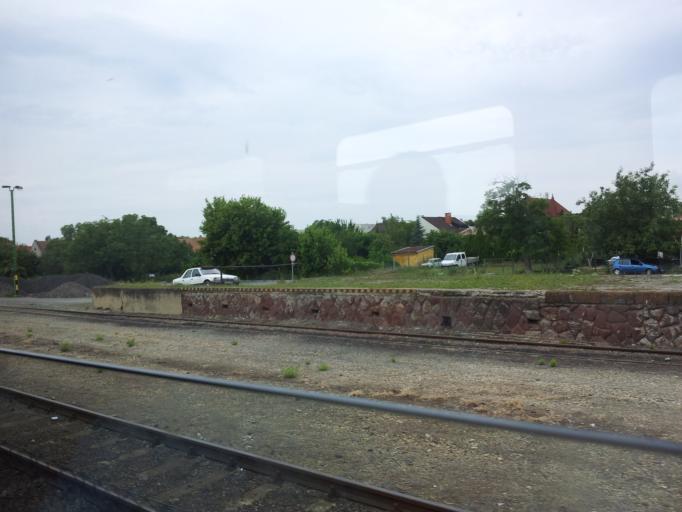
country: HU
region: Veszprem
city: Balatonfured
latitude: 46.9567
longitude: 17.8835
